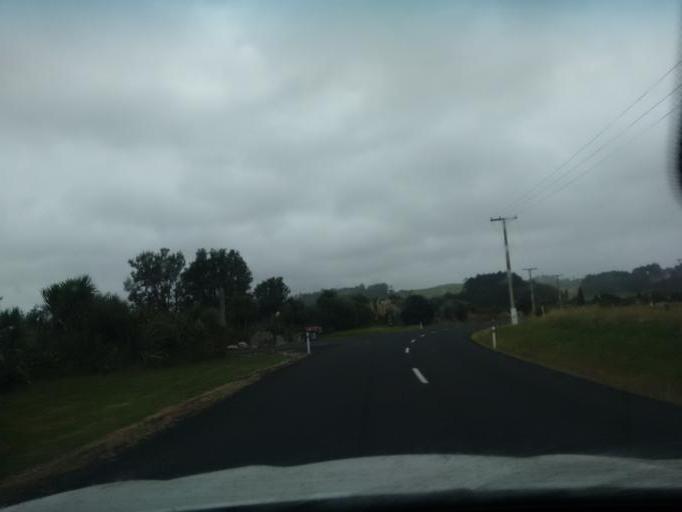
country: NZ
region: Waikato
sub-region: Thames-Coromandel District
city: Whitianga
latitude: -36.8692
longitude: 175.8063
